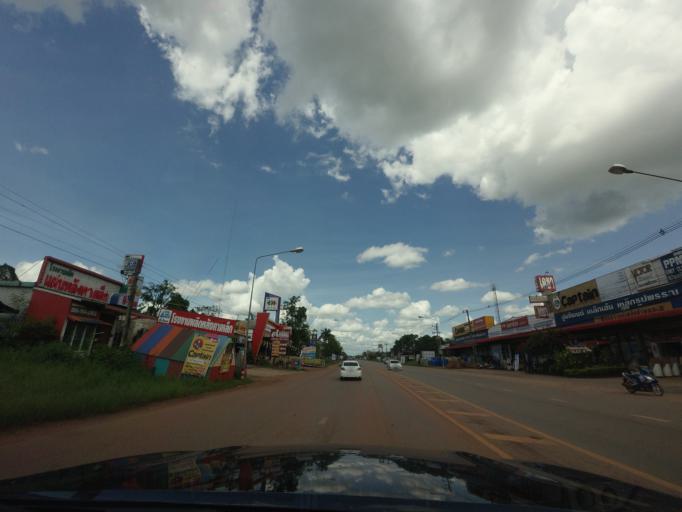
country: TH
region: Changwat Udon Thani
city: Ban Dung
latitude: 17.6795
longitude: 103.2545
